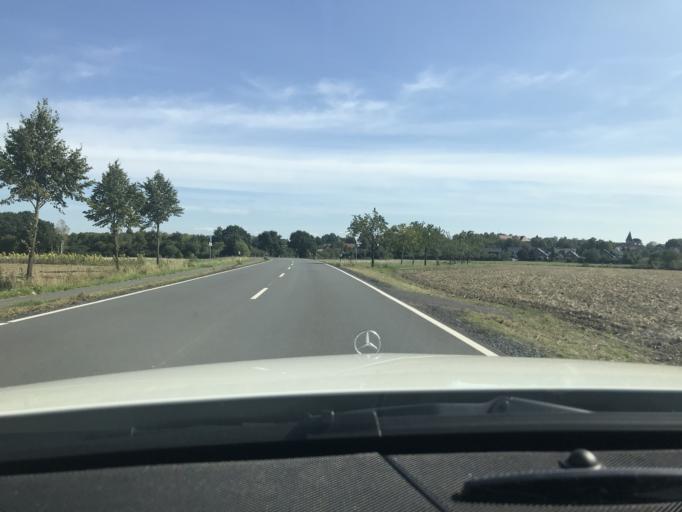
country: DE
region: North Rhine-Westphalia
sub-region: Regierungsbezirk Arnsberg
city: Bonen
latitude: 51.6055
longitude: 7.7726
